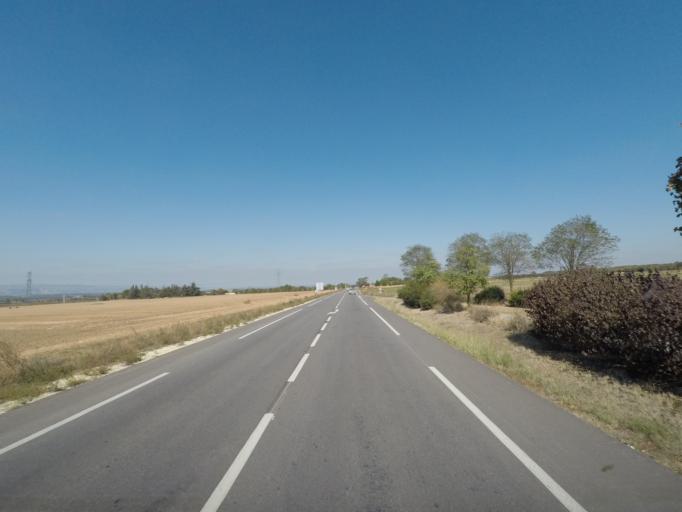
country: FR
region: Rhone-Alpes
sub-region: Departement de la Drome
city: Montmeyran
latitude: 44.8431
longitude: 5.0090
